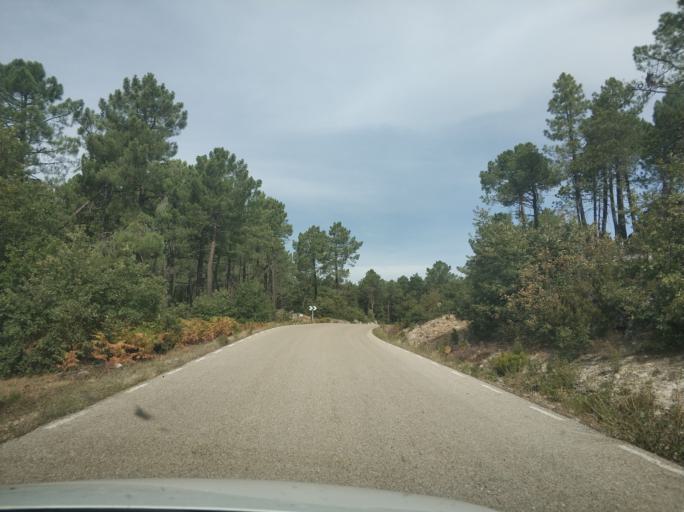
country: ES
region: Castille and Leon
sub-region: Provincia de Soria
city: Duruelo de la Sierra
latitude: 41.8897
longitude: -2.9412
